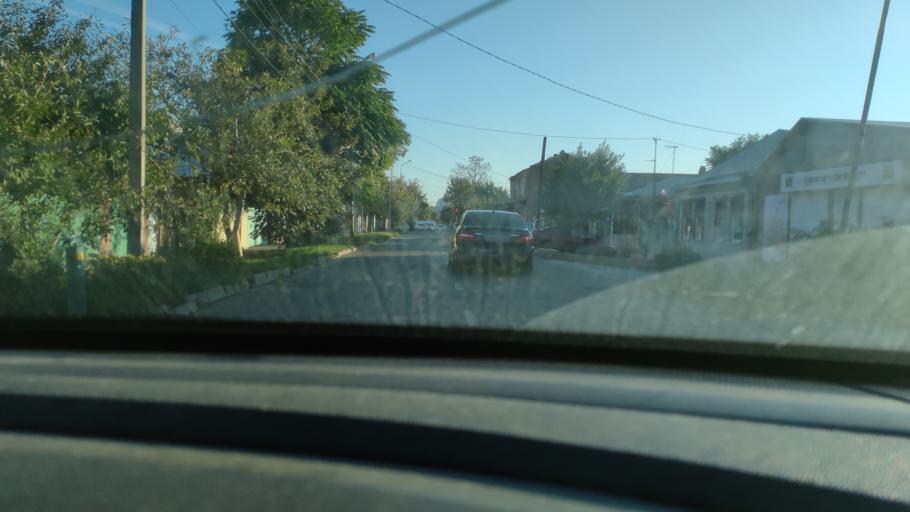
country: RU
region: Krasnodarskiy
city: Krasnodar
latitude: 45.0403
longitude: 38.9646
